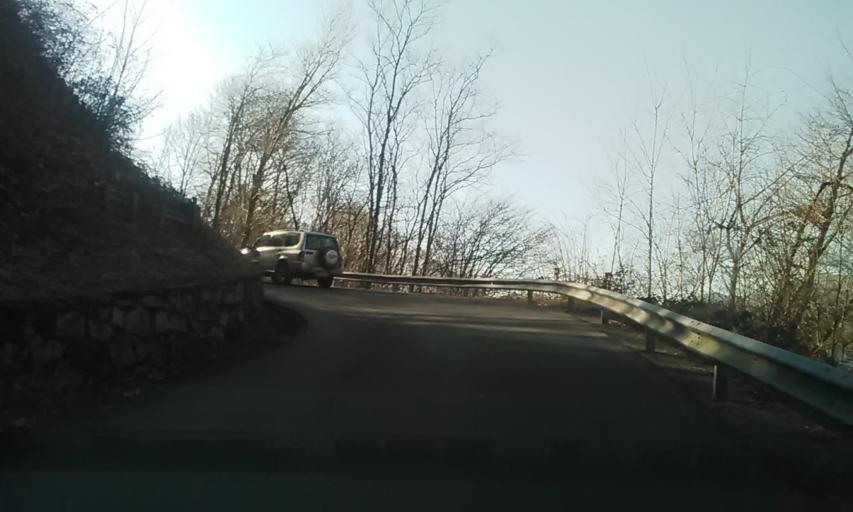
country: IT
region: Piedmont
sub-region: Provincia di Vercelli
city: Quarona
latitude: 45.7616
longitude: 8.2784
